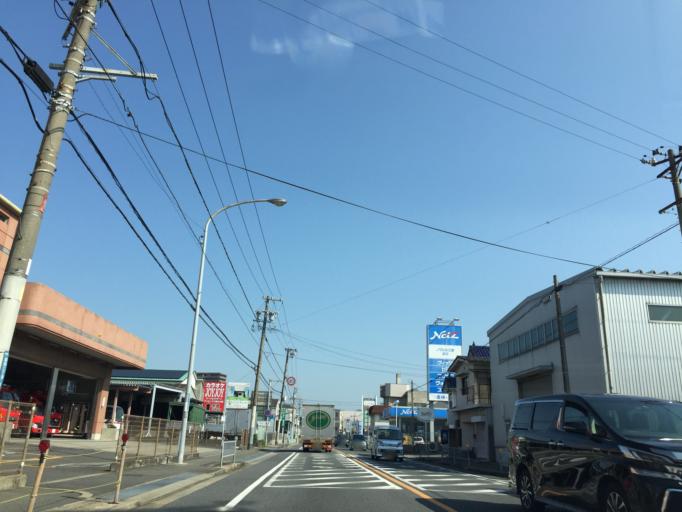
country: JP
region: Mie
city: Yokkaichi
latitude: 35.0050
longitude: 136.6553
